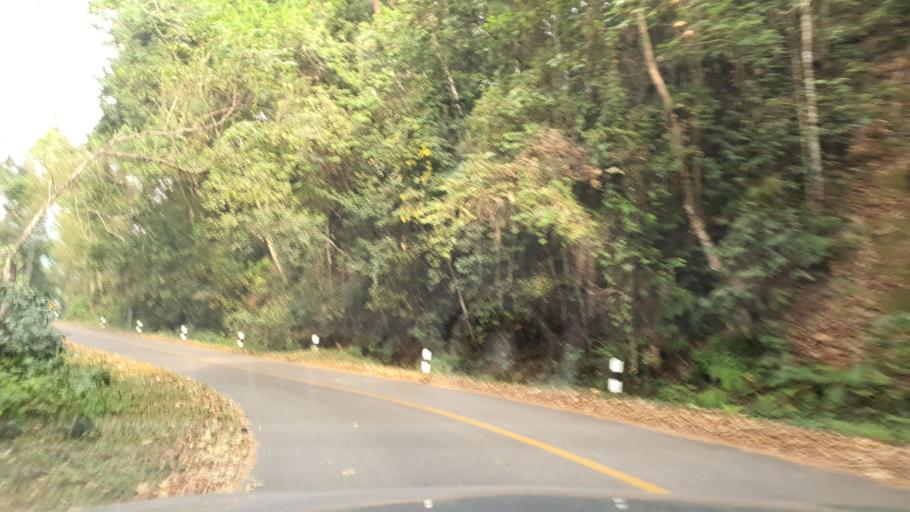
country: TH
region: Chiang Mai
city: Mae On
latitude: 18.9413
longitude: 99.3590
